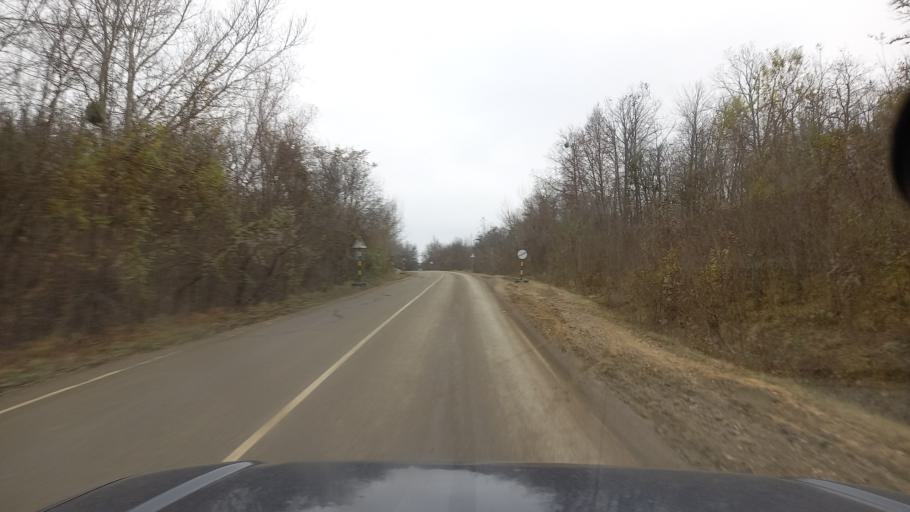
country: RU
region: Krasnodarskiy
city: Goryachiy Klyuch
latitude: 44.5546
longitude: 39.2522
